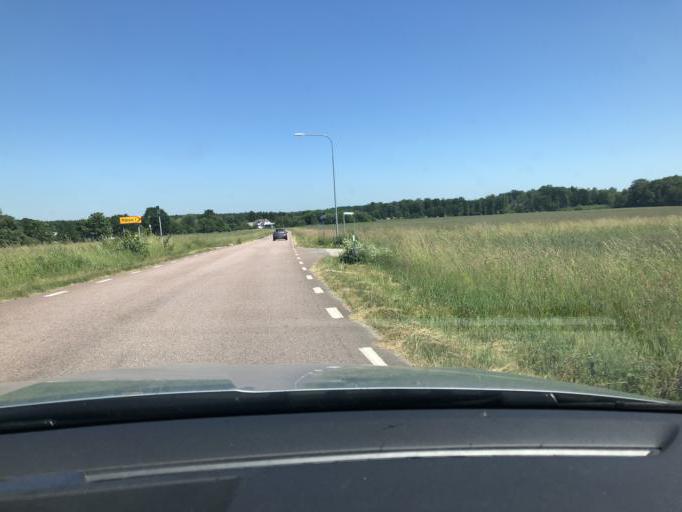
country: SE
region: Blekinge
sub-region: Olofstroms Kommun
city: Jamshog
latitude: 56.1769
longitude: 14.6093
